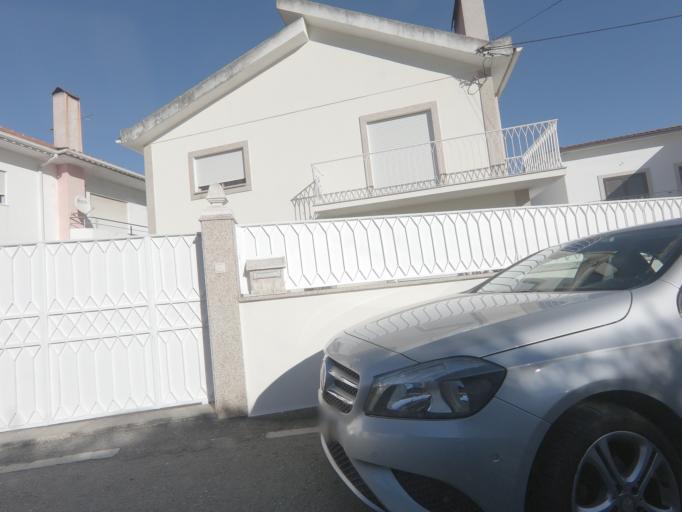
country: PT
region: Vila Real
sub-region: Peso da Regua
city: Peso da Regua
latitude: 41.1686
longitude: -7.7807
